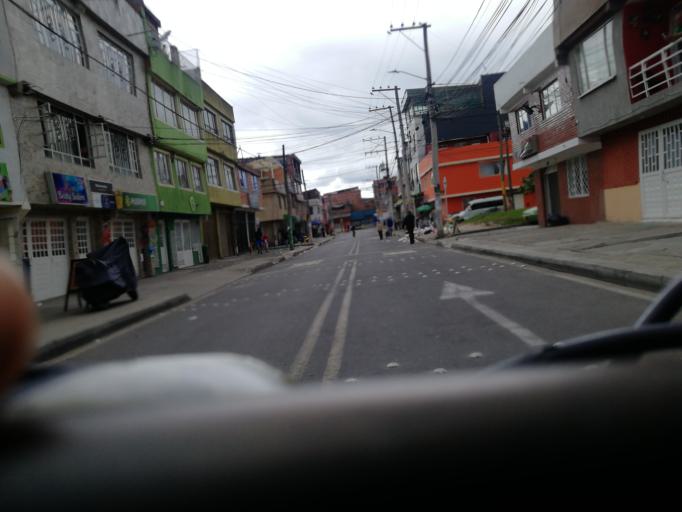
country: CO
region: Cundinamarca
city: Soacha
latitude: 4.6107
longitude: -74.1642
